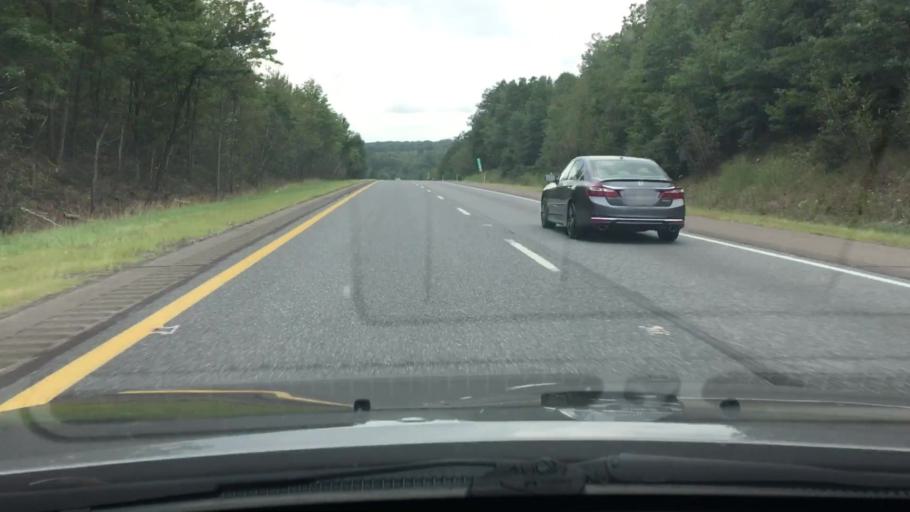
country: US
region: Pennsylvania
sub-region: Schuylkill County
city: Tremont
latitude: 40.7003
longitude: -76.3665
